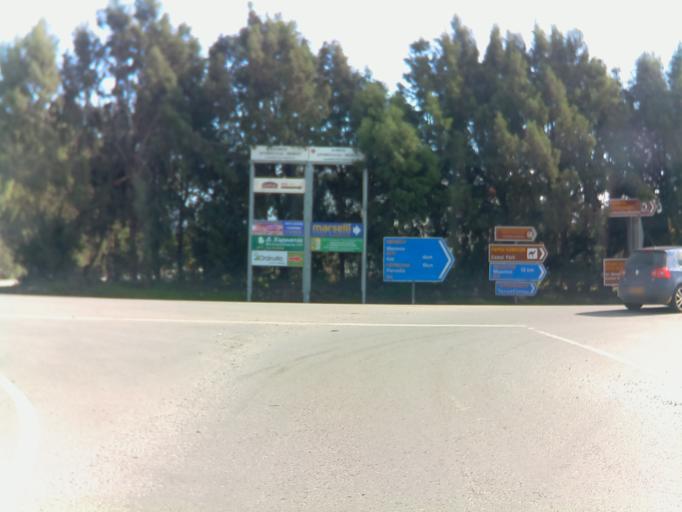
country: CY
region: Larnaka
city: Meneou
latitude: 34.8668
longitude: 33.5991
